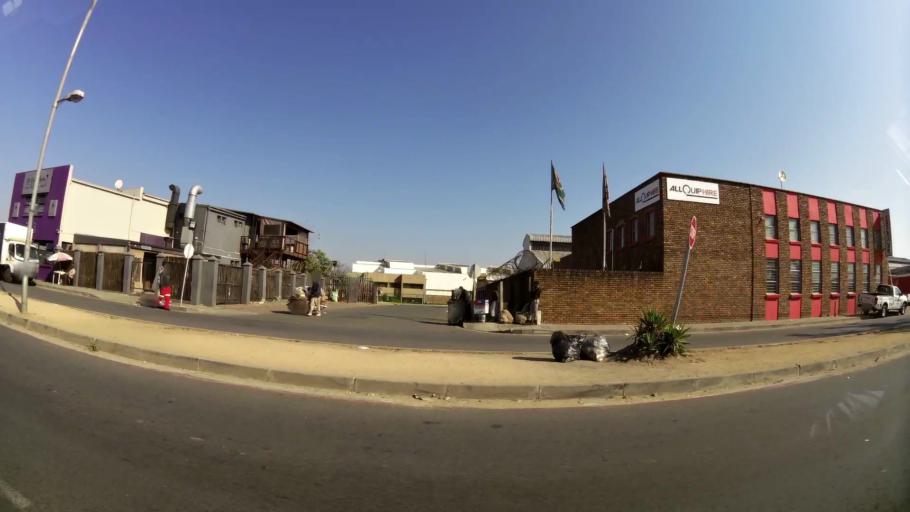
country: ZA
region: Gauteng
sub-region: City of Johannesburg Metropolitan Municipality
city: Modderfontein
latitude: -26.0997
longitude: 28.0855
